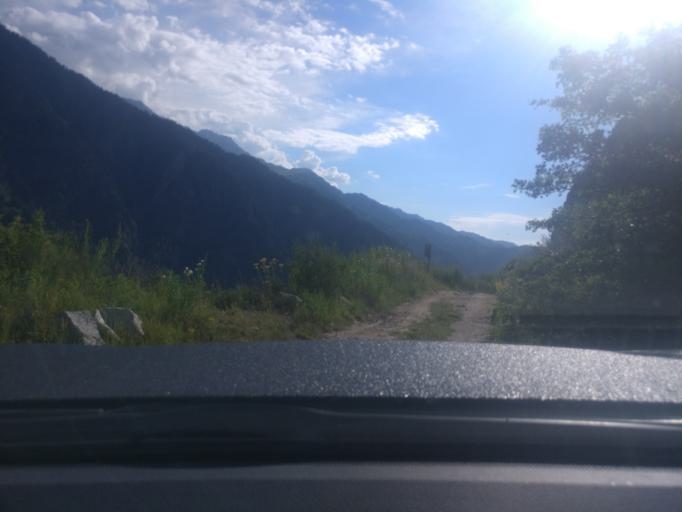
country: KZ
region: Almaty Qalasy
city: Almaty
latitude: 43.1063
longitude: 76.9451
